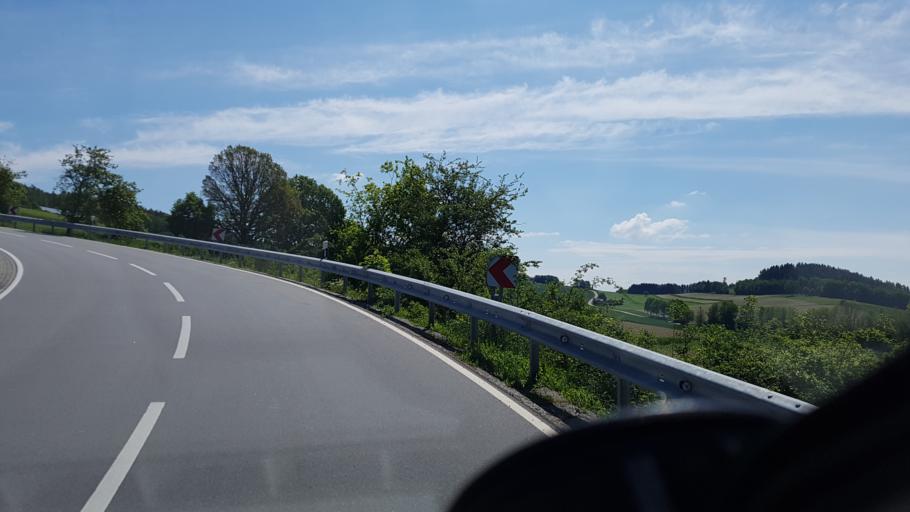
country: DE
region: Bavaria
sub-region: Lower Bavaria
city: Triftern
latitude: 48.3930
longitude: 13.0177
